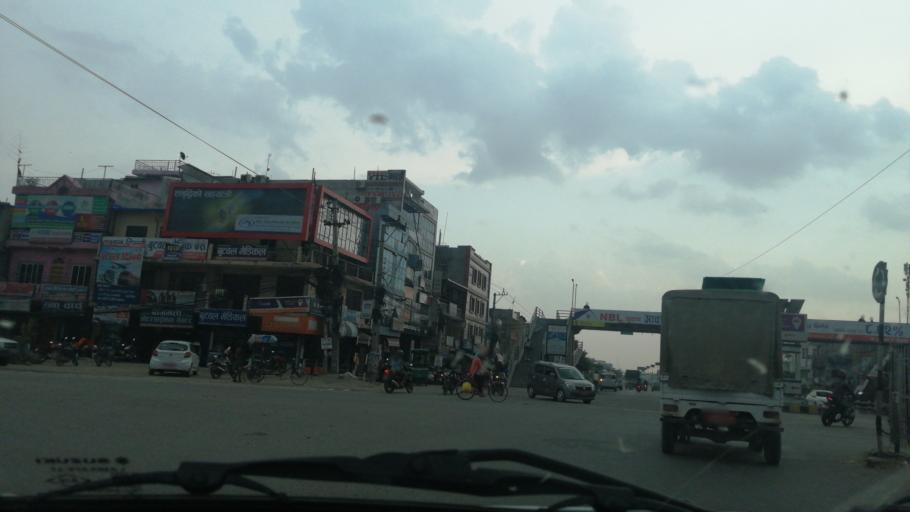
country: NP
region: Western Region
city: Butwal
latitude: 27.6829
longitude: 83.4649
